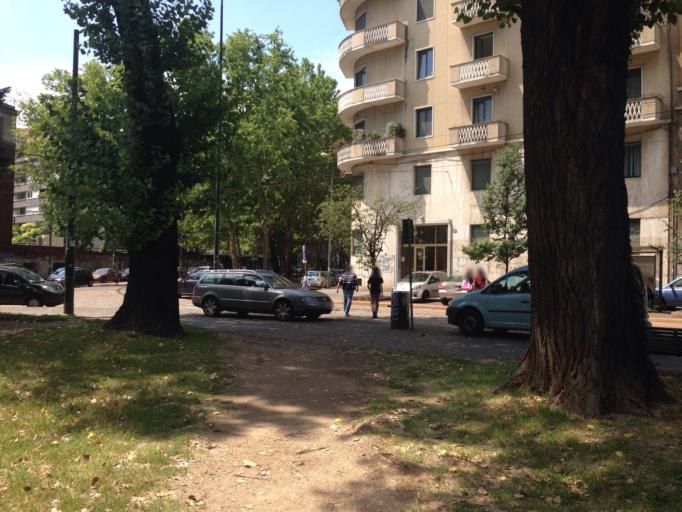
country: IT
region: Lombardy
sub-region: Citta metropolitana di Milano
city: Milano
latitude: 45.4773
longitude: 9.2259
